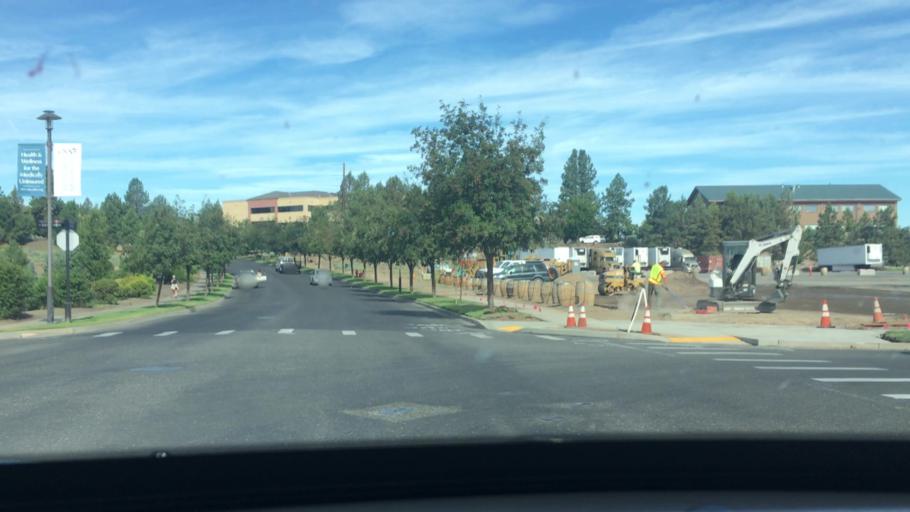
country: US
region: Oregon
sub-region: Deschutes County
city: Bend
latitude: 44.0438
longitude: -121.3205
